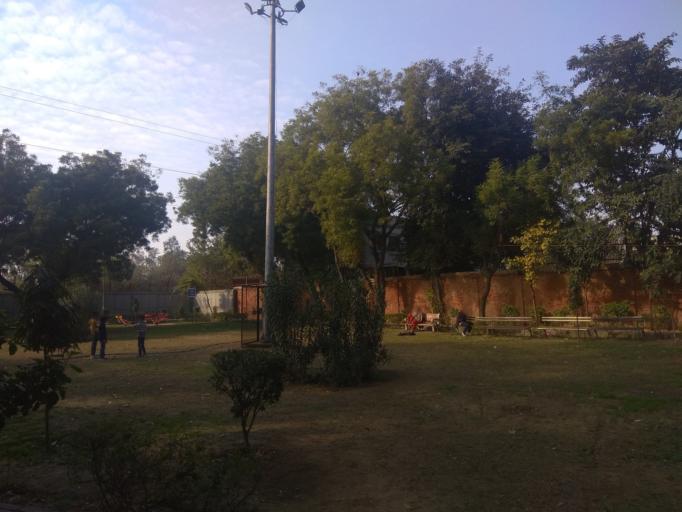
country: IN
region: NCT
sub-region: West Delhi
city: Nangloi Jat
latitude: 28.6293
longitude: 77.0662
